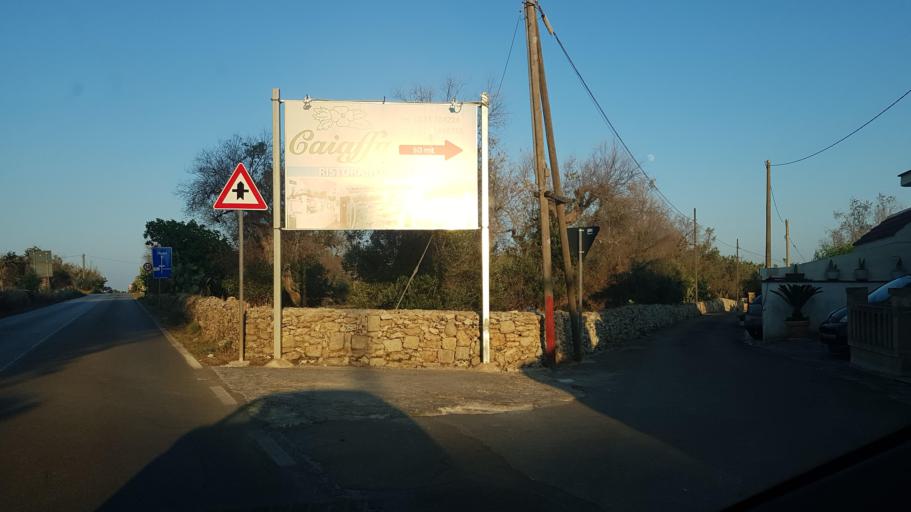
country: IT
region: Apulia
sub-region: Provincia di Lecce
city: Lucugnano
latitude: 39.9384
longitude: 18.3119
